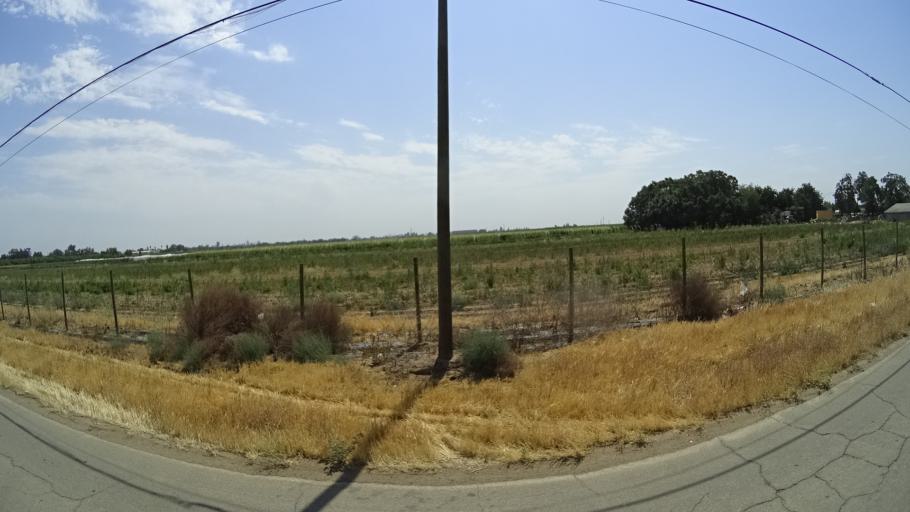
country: US
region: California
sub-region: Fresno County
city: West Park
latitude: 36.7172
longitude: -119.8359
